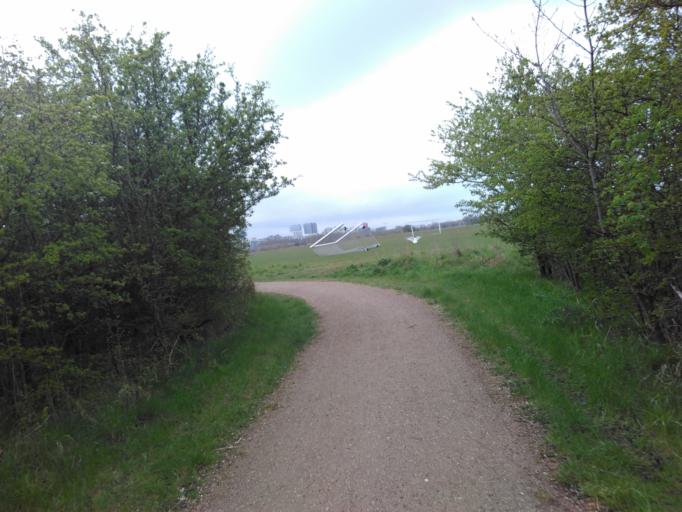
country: DK
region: Capital Region
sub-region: Kobenhavn
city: Copenhagen
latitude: 55.6463
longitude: 12.5690
